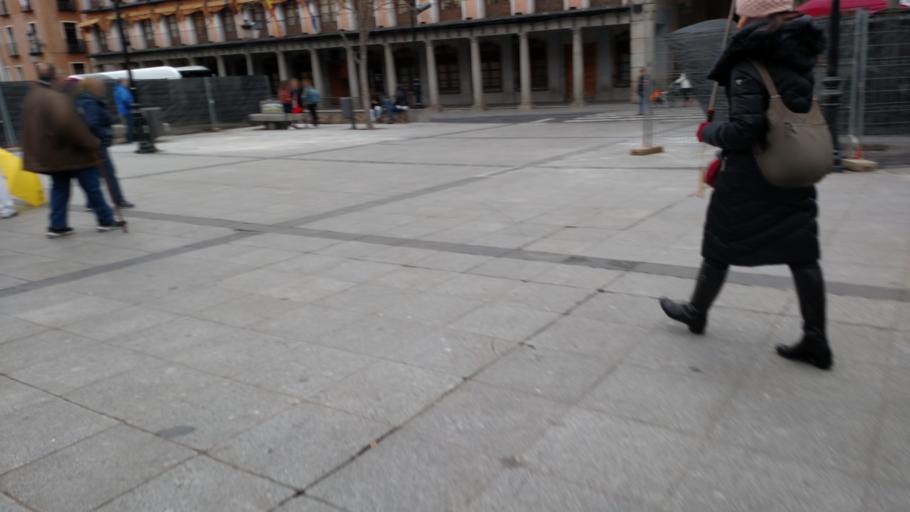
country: ES
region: Castille-La Mancha
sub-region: Province of Toledo
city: Toledo
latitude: 39.8594
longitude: -4.0214
